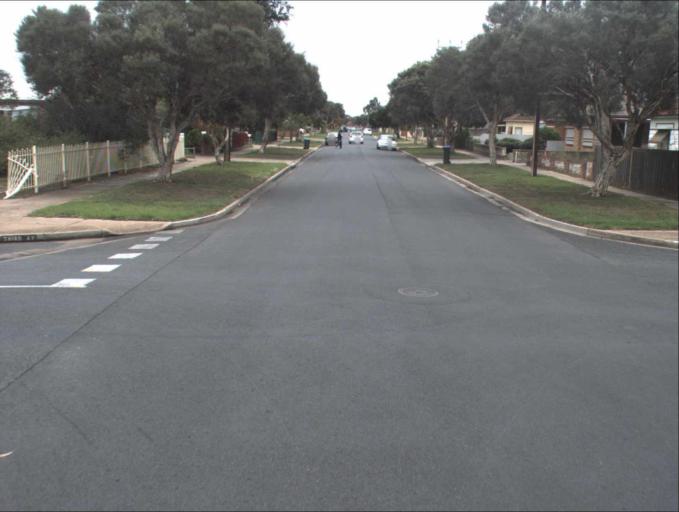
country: AU
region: South Australia
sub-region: Charles Sturt
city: Woodville North
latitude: -34.8704
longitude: 138.5544
